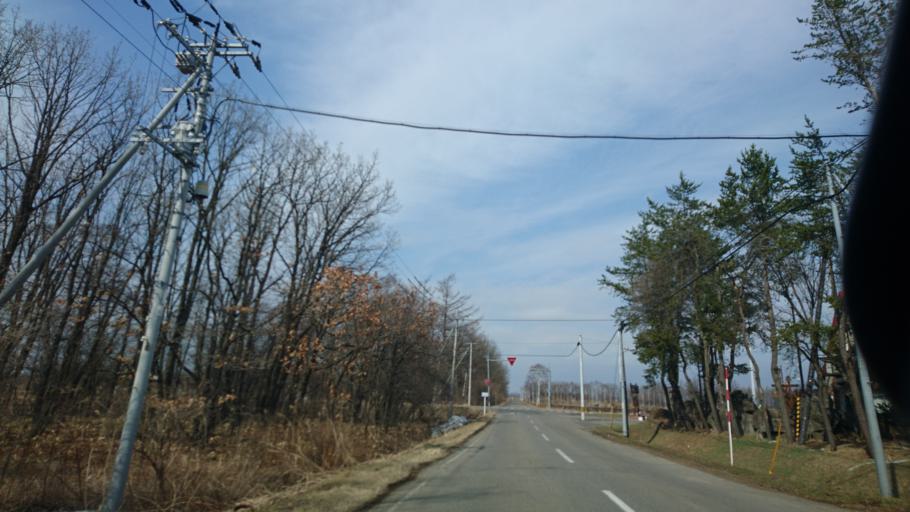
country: JP
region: Hokkaido
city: Otofuke
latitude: 43.0807
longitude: 143.2272
